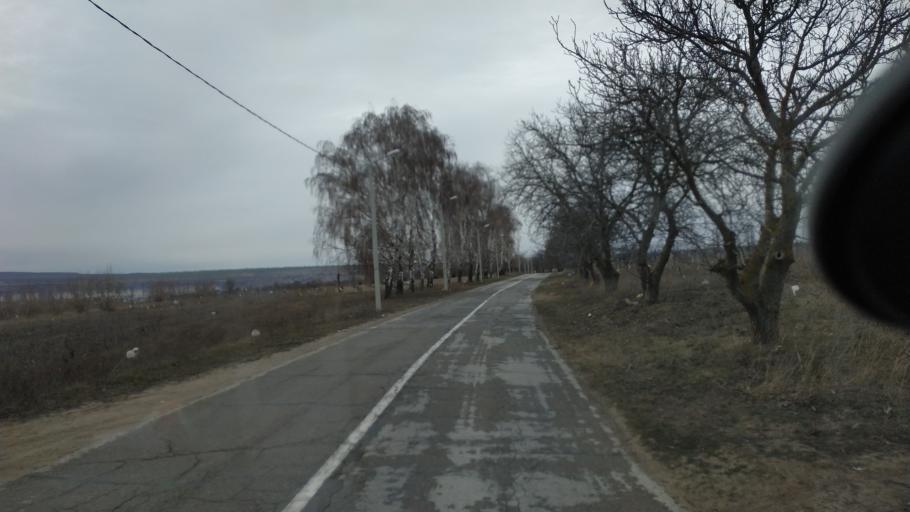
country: MD
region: Telenesti
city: Cocieri
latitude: 47.3325
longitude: 29.0971
